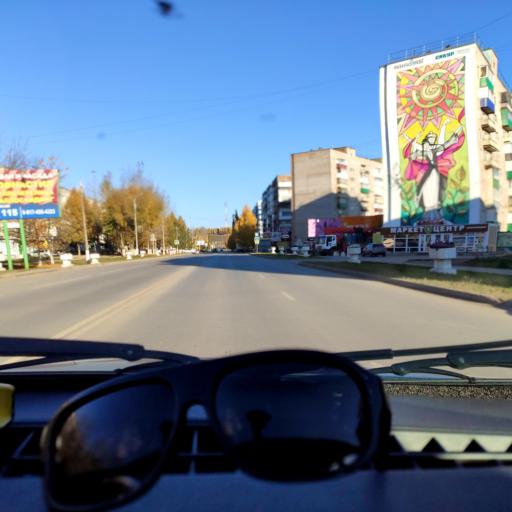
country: RU
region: Bashkortostan
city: Blagoveshchensk
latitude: 55.0492
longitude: 55.9554
